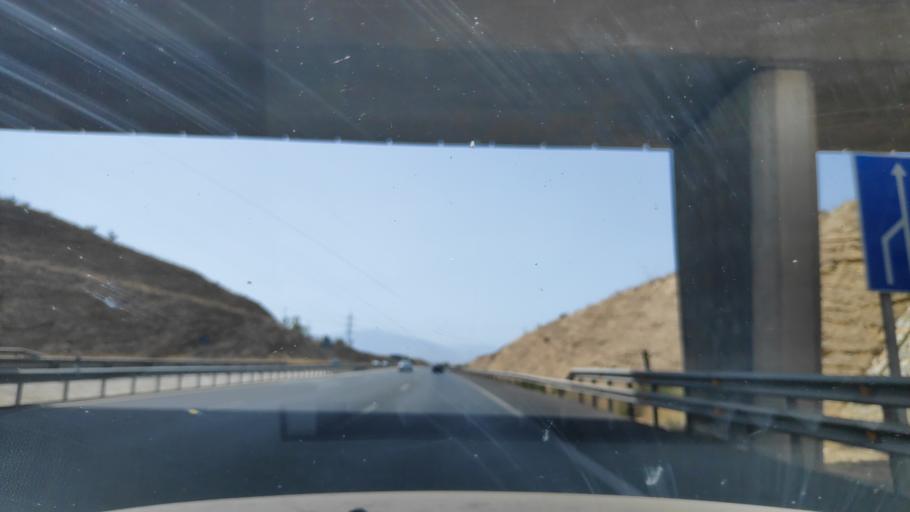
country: ES
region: Murcia
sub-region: Murcia
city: Molina de Segura
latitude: 38.0463
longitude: -1.1678
